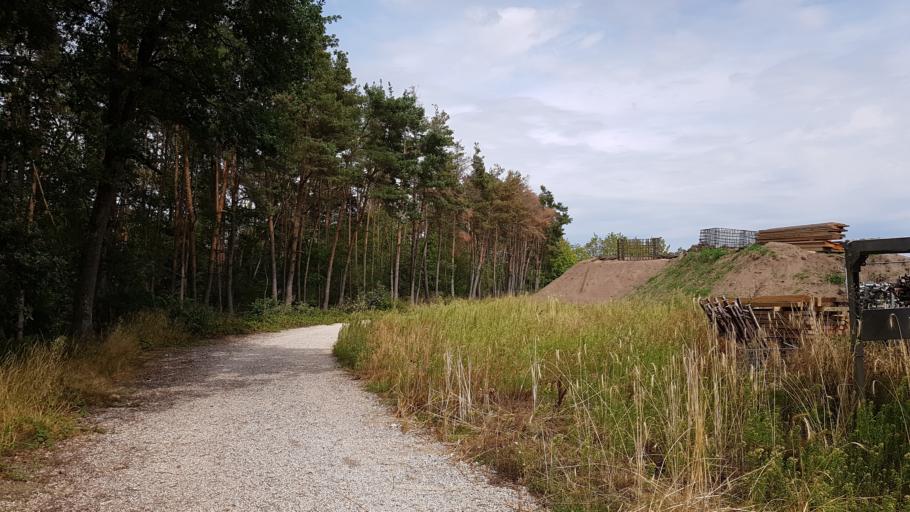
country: DE
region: Bavaria
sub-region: Regierungsbezirk Mittelfranken
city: Hilpoltstein
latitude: 49.1947
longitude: 11.1753
